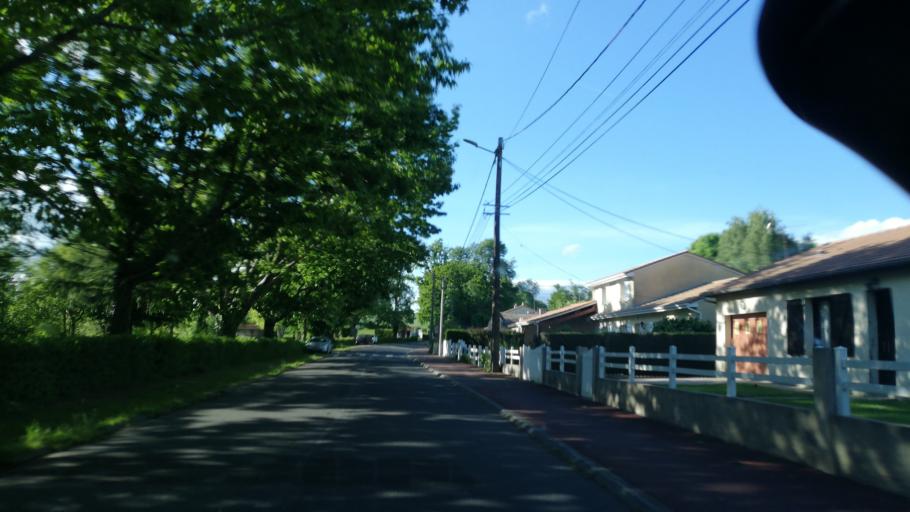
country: FR
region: Poitou-Charentes
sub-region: Departement des Deux-Sevres
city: Boisme
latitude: 46.7763
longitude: -0.4330
